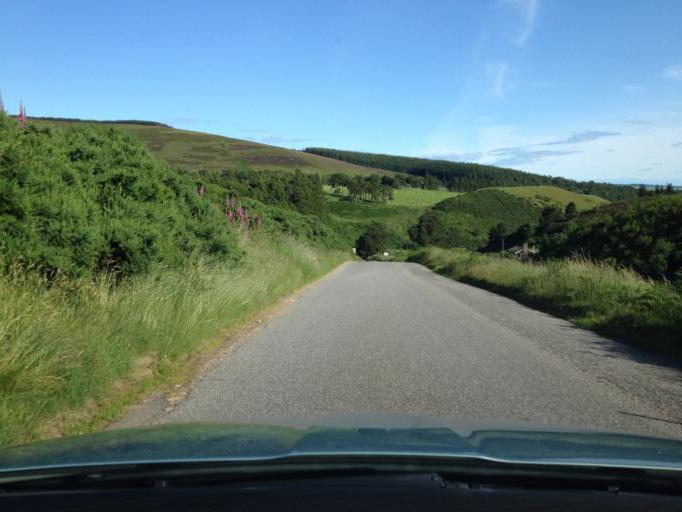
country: GB
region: Scotland
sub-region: Aberdeenshire
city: Laurencekirk
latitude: 56.8961
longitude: -2.5547
